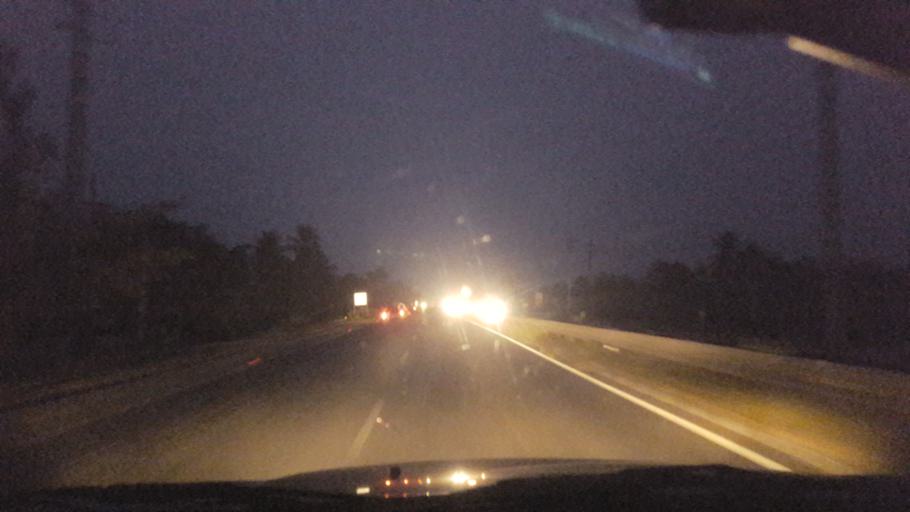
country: IN
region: Andhra Pradesh
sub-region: East Godavari
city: Peddapuram
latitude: 17.1341
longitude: 81.9541
